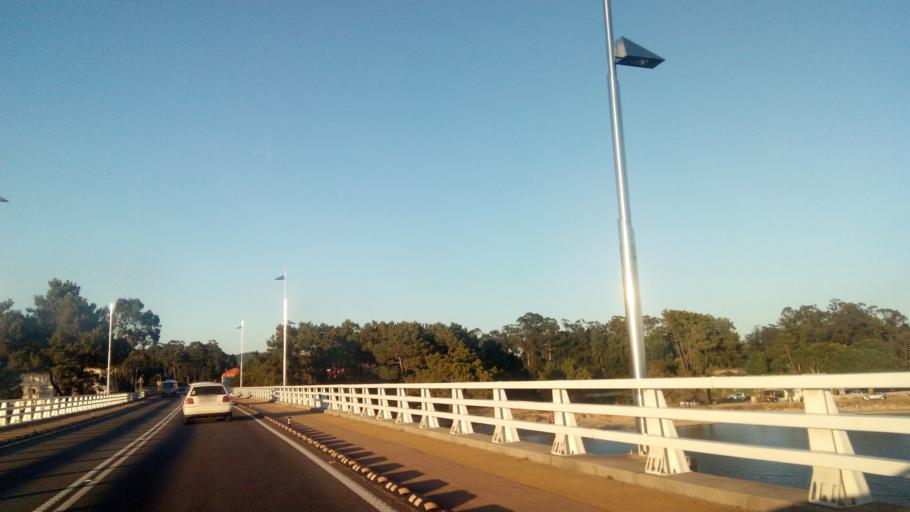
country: ES
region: Galicia
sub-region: Provincia de Pontevedra
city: Vilanova de Arousa
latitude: 42.5483
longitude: -8.8342
